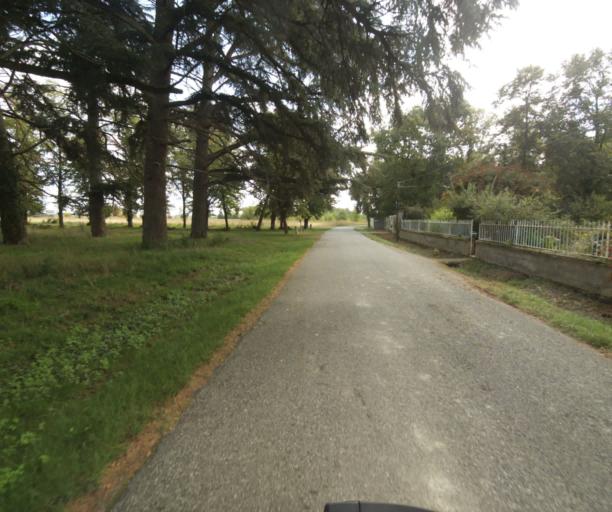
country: FR
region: Midi-Pyrenees
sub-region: Departement du Tarn-et-Garonne
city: Finhan
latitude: 43.9281
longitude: 1.2176
